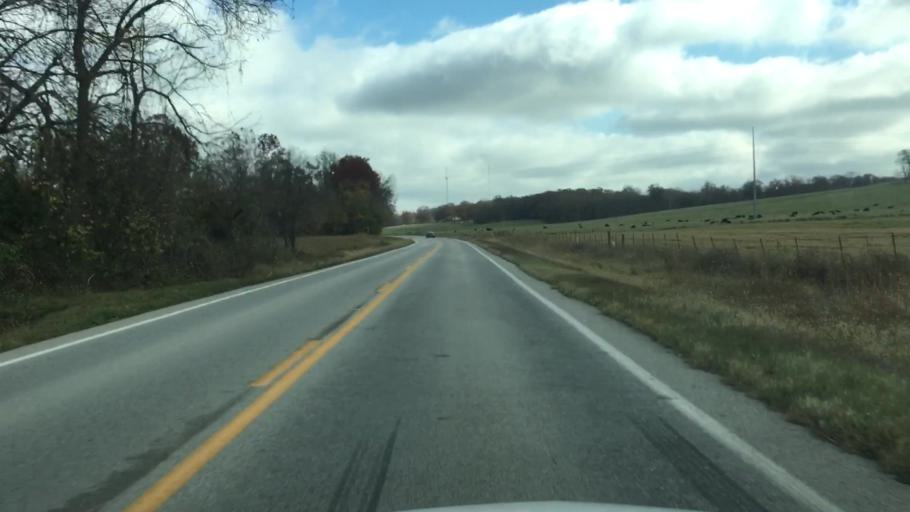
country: US
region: Arkansas
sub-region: Benton County
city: Gentry
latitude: 36.2581
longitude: -94.4062
